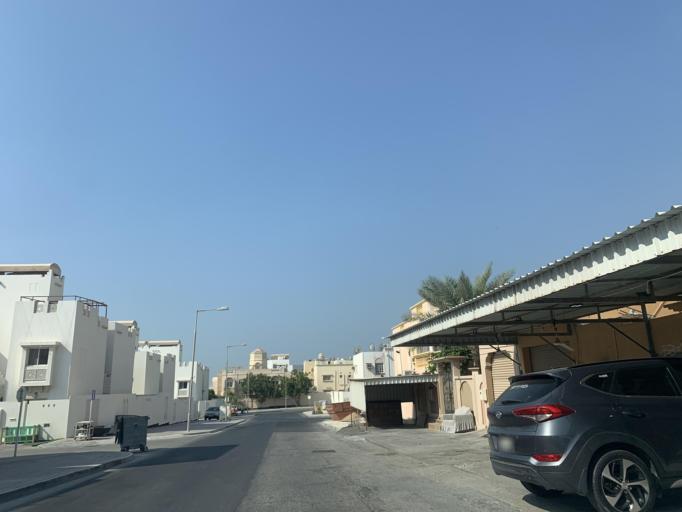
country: BH
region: Central Governorate
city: Madinat Hamad
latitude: 26.1012
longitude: 50.5029
